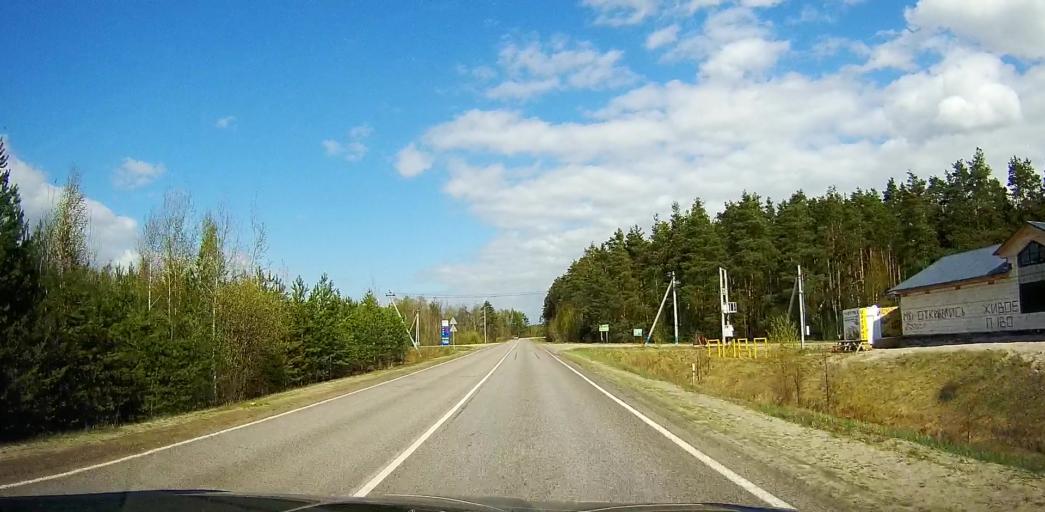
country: RU
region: Moskovskaya
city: Davydovo
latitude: 55.5492
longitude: 38.8171
